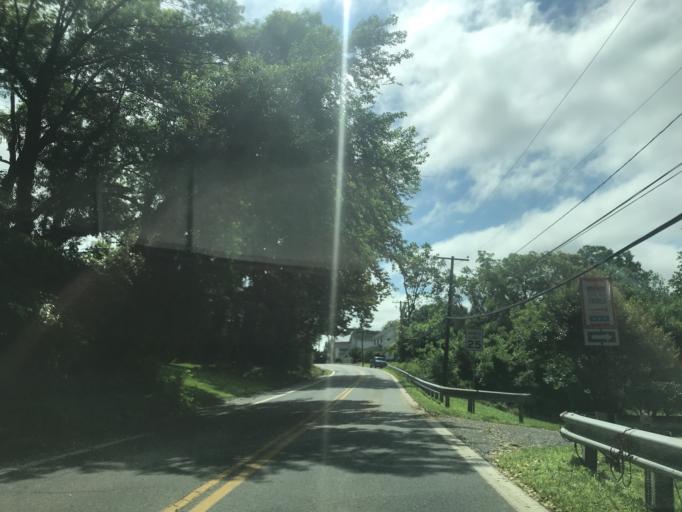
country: US
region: Maryland
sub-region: Caroline County
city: Ridgely
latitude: 38.9174
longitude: -75.9451
